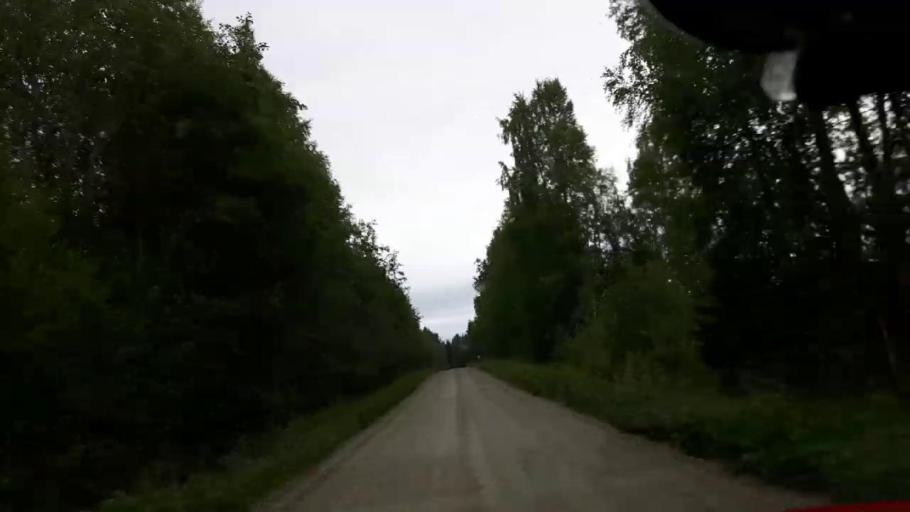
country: SE
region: Vaesternorrland
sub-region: Ange Kommun
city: Ange
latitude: 62.8000
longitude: 15.7704
